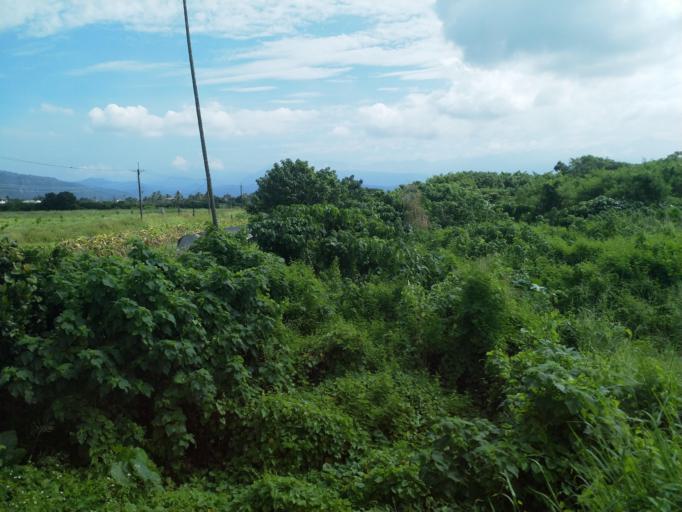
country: TW
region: Taiwan
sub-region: Pingtung
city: Pingtung
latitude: 22.8760
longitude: 120.4976
